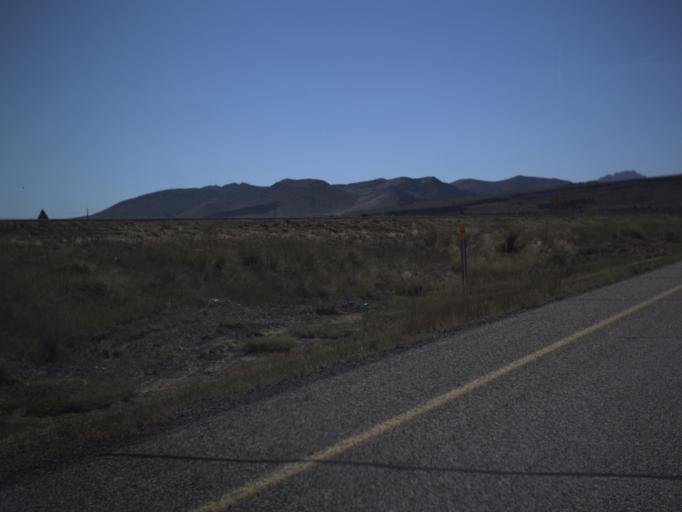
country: US
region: Utah
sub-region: Beaver County
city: Beaver
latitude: 38.5862
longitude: -112.5868
